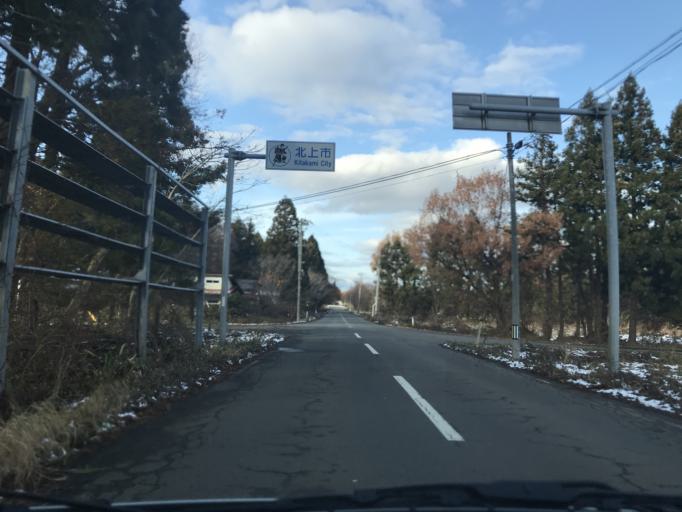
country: JP
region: Iwate
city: Kitakami
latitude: 39.2520
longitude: 141.0325
